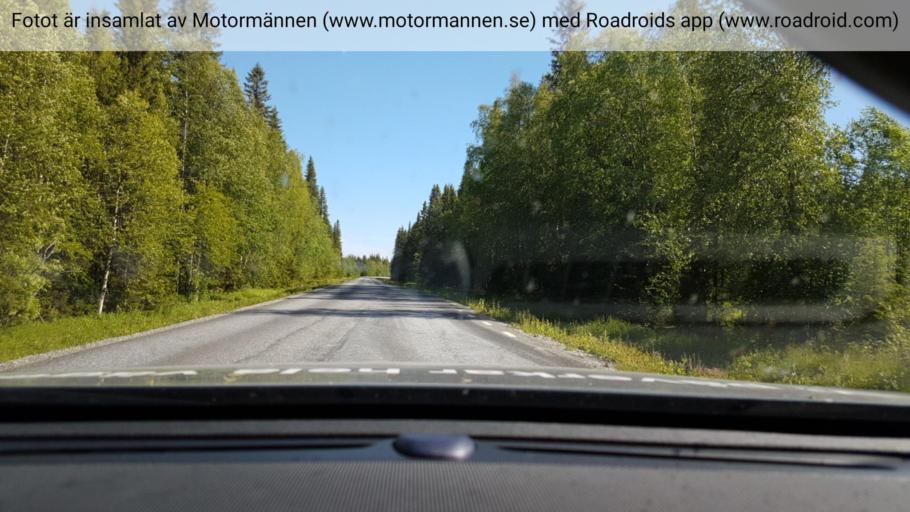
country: SE
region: Vaesterbotten
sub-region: Vilhelmina Kommun
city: Sjoberg
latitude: 64.7384
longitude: 16.2086
